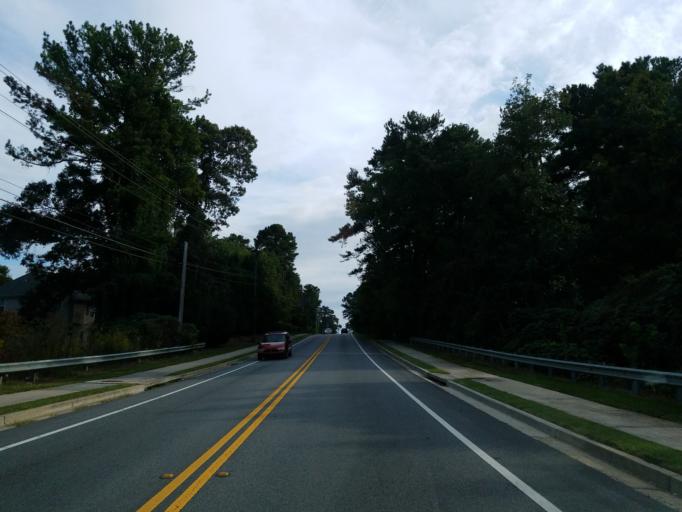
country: US
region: Georgia
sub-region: Cobb County
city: Kennesaw
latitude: 34.0390
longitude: -84.5507
